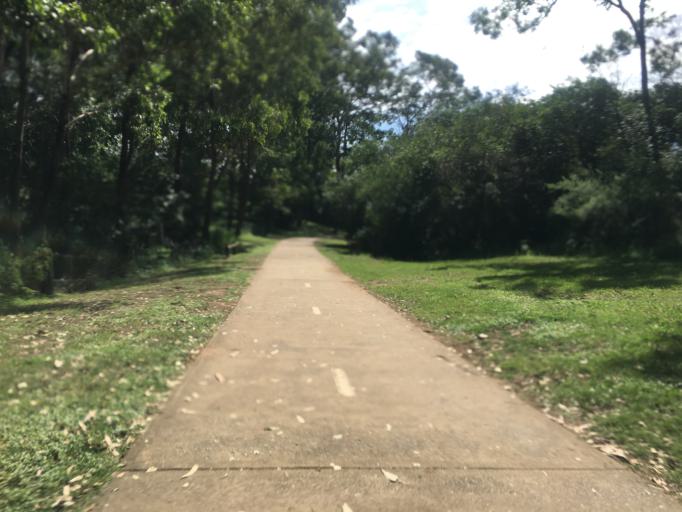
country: AU
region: New South Wales
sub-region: Camden
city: Camden South
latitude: -34.0764
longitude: 150.7017
